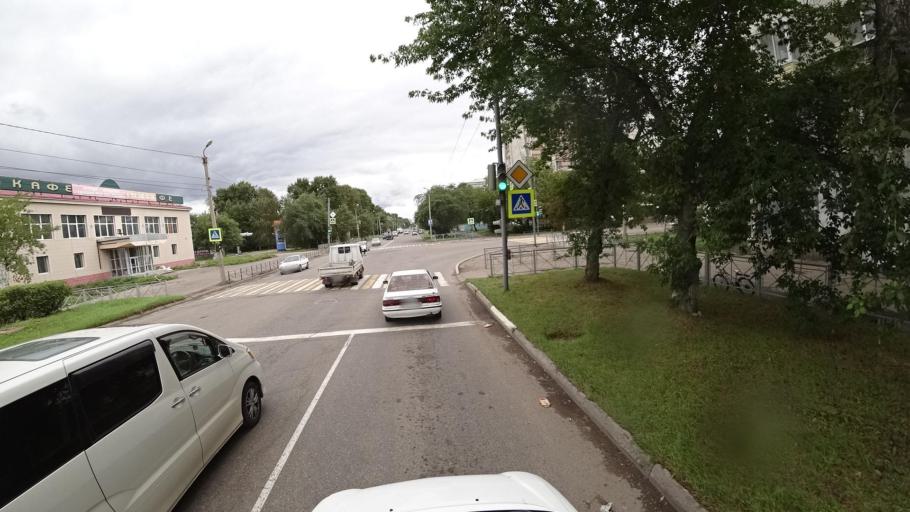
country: RU
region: Khabarovsk Krai
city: Komsomolsk-on-Amur
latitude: 50.5532
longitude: 137.0265
